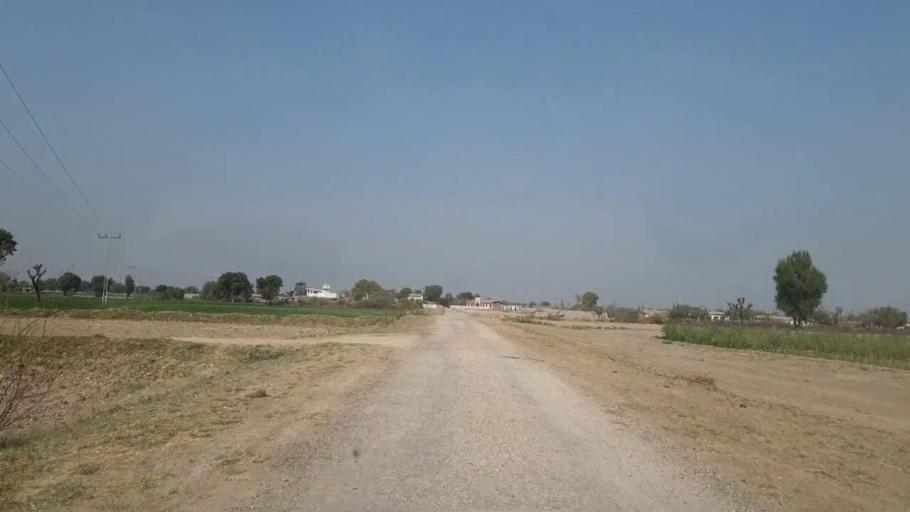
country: PK
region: Sindh
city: Mirpur Khas
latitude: 25.6522
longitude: 69.1105
